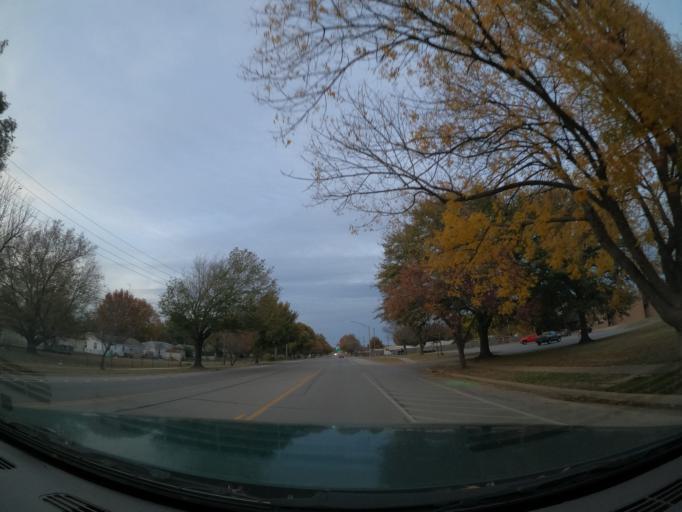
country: US
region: Oklahoma
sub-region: Tulsa County
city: Broken Arrow
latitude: 36.0347
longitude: -95.7908
